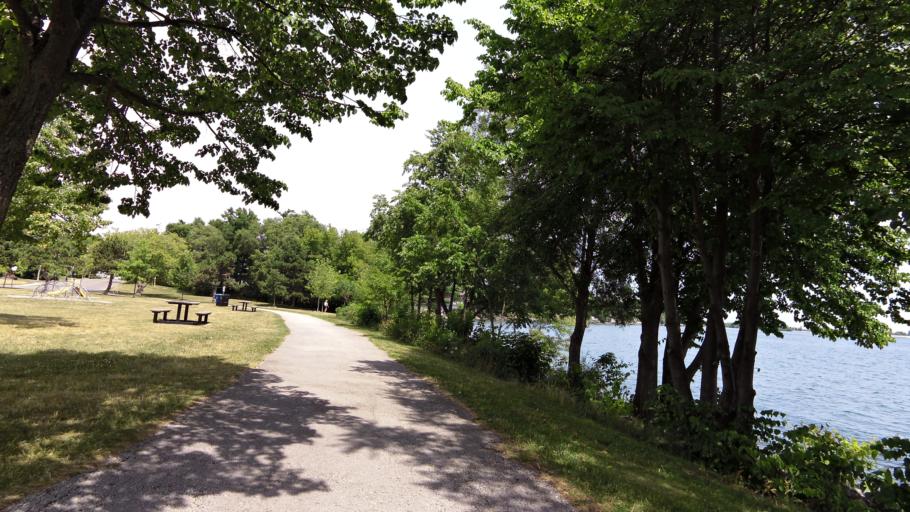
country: CA
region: Ontario
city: Etobicoke
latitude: 43.5883
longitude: -79.5294
